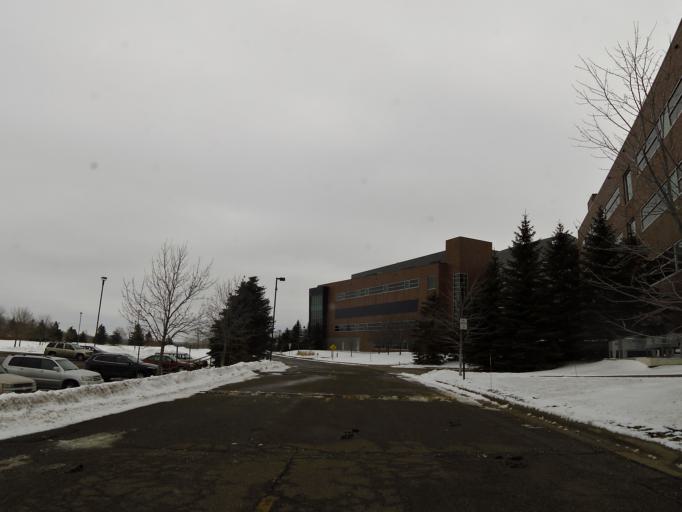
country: US
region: Minnesota
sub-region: Washington County
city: Oakdale
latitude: 45.0010
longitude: -92.9497
